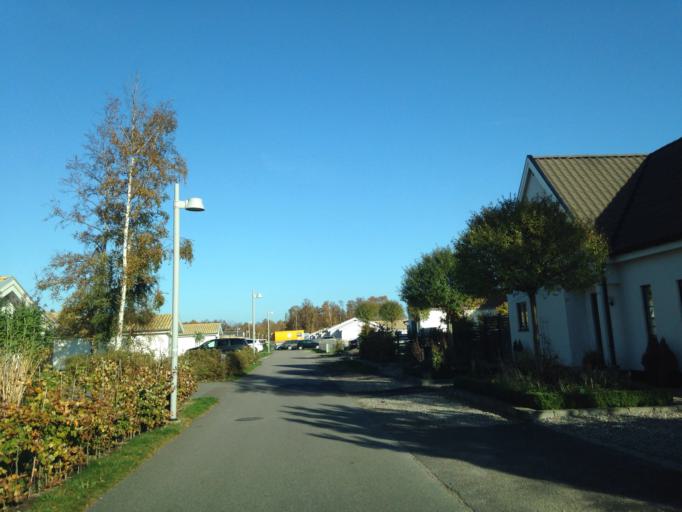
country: SE
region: Skane
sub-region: Vellinge Kommun
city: Skanor med Falsterbo
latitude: 55.3976
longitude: 12.8458
